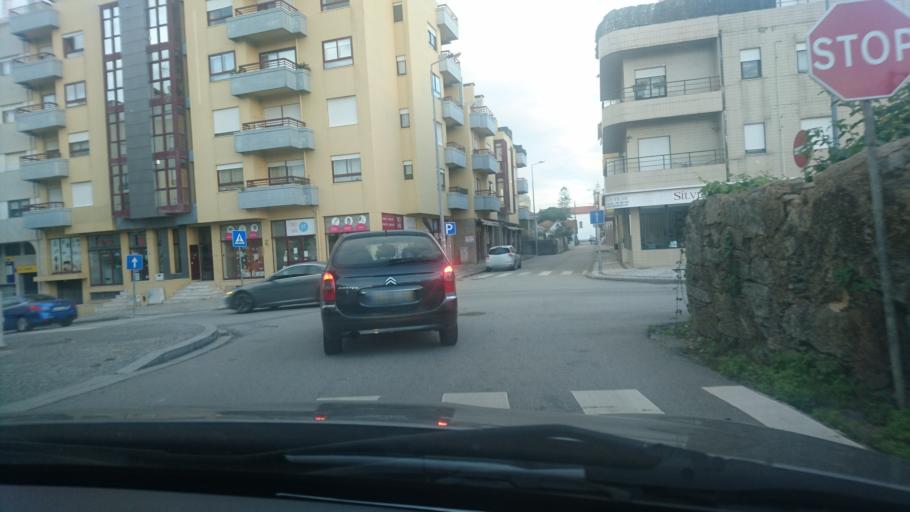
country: PT
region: Aveiro
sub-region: Sao Joao da Madeira
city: Sao Joao da Madeira
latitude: 40.8938
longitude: -8.4913
